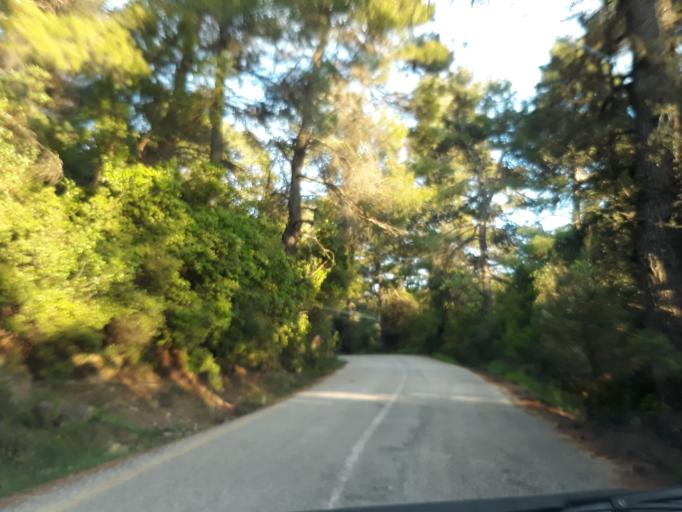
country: GR
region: Attica
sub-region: Nomarchia Anatolikis Attikis
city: Afidnes
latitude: 38.2183
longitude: 23.7802
